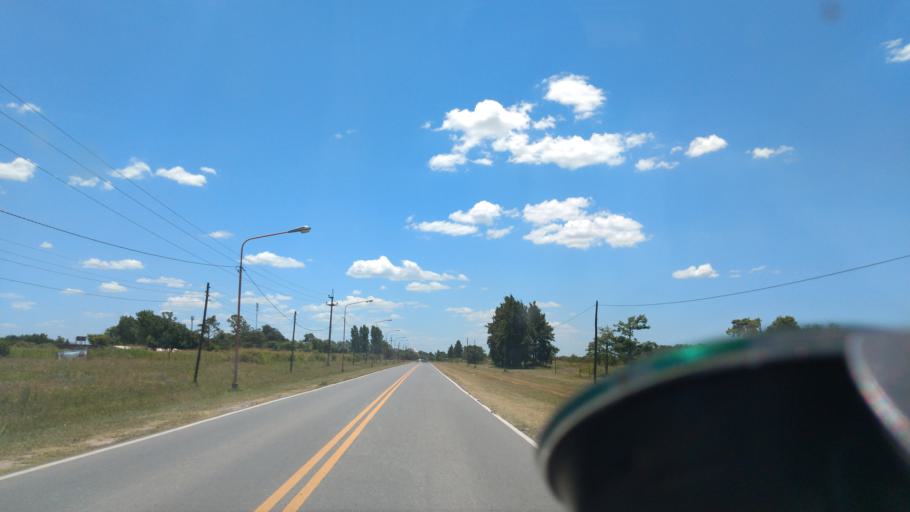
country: AR
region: Santa Fe
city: Laguna Paiva
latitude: -31.3258
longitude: -60.6591
